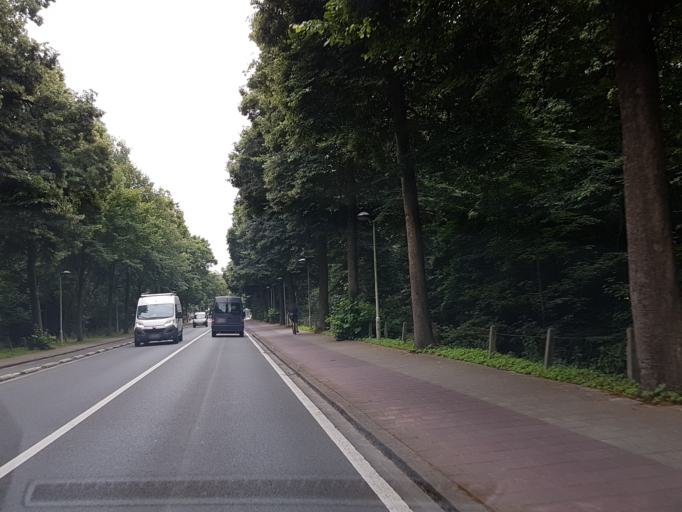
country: BE
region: Flanders
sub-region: Provincie Antwerpen
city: Borsbeek
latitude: 51.2170
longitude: 4.4617
